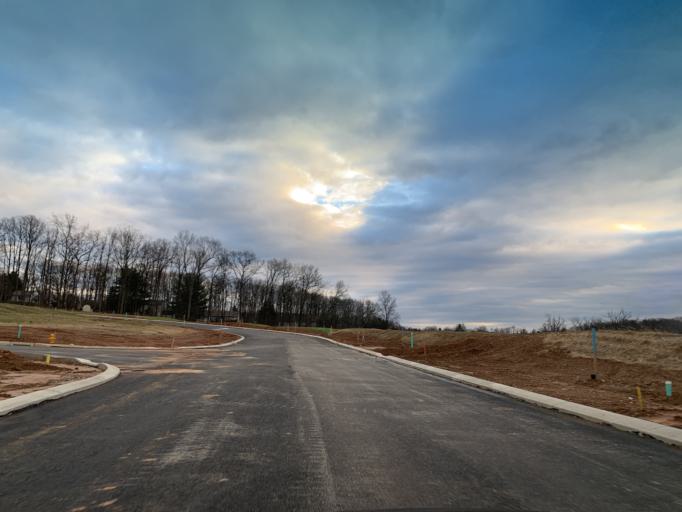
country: US
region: Pennsylvania
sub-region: York County
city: Stewartstown
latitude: 39.7681
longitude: -76.5941
